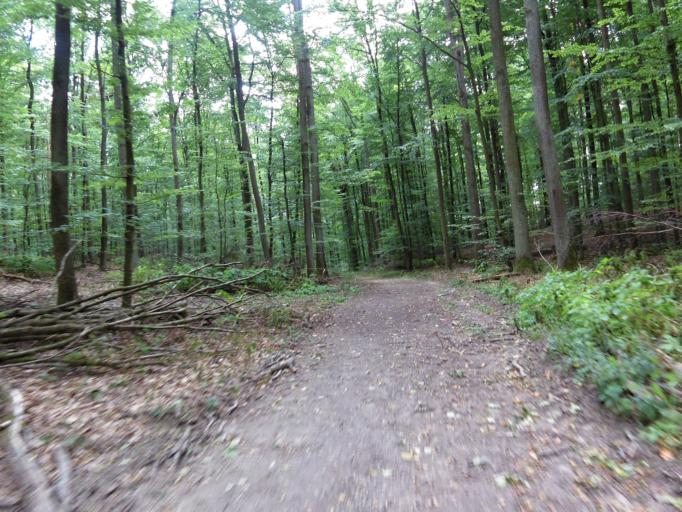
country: DE
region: Bavaria
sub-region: Regierungsbezirk Unterfranken
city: Waldbuttelbrunn
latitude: 49.7870
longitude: 9.8633
